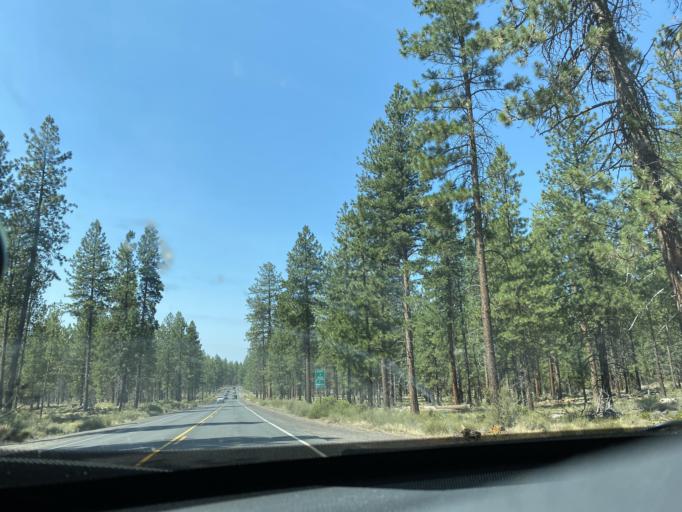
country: US
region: Oregon
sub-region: Deschutes County
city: Sunriver
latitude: 43.8904
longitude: -121.3900
